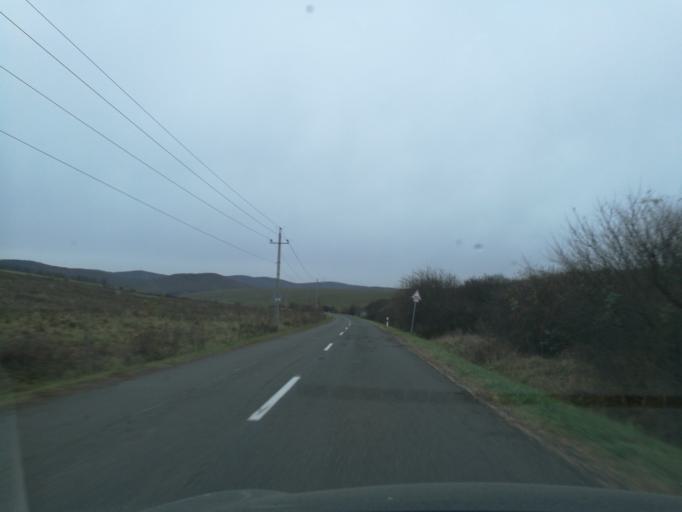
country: HU
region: Nograd
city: Rimoc
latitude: 48.0149
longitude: 19.5979
